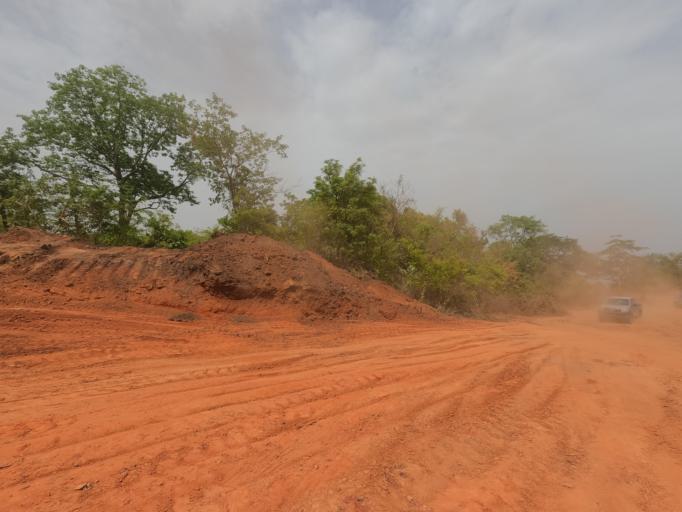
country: GW
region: Oio
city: Bissora
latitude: 12.4531
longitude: -15.4965
